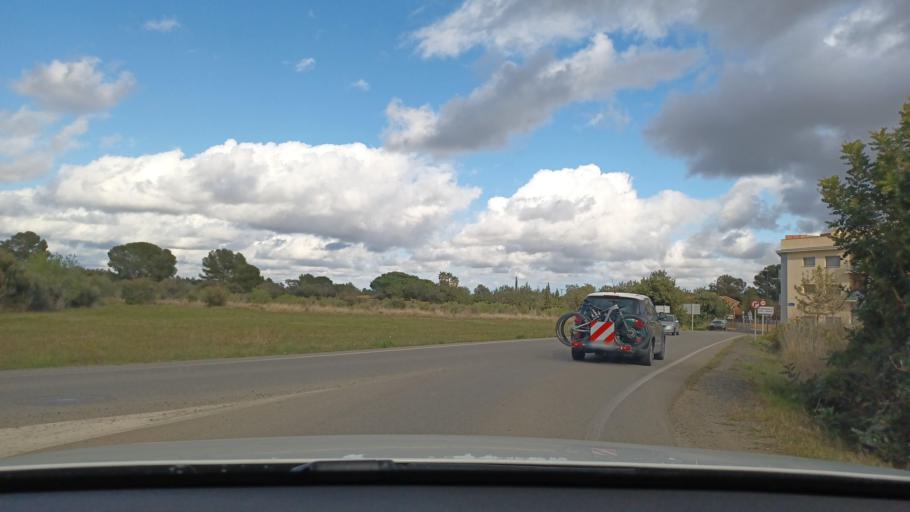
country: ES
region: Catalonia
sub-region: Provincia de Tarragona
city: Botarell
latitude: 41.1239
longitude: 0.9986
